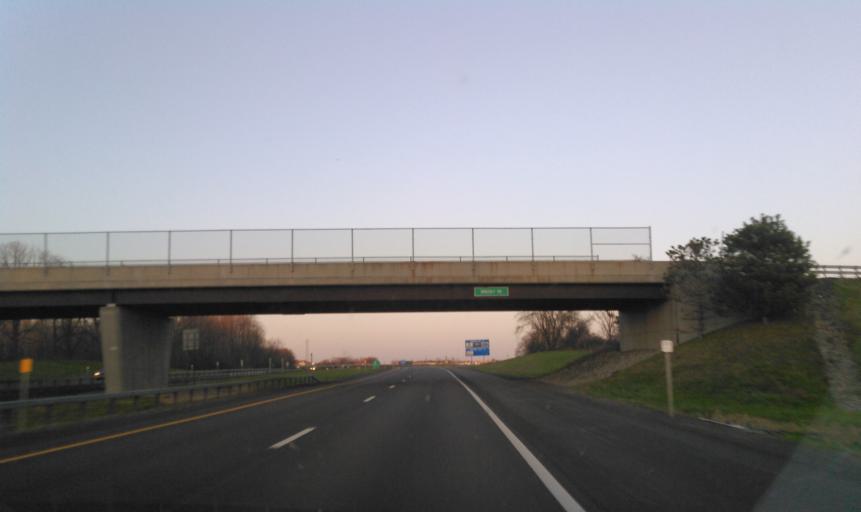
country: US
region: New York
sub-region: Seneca County
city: Waterloo
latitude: 42.9654
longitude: -76.8658
